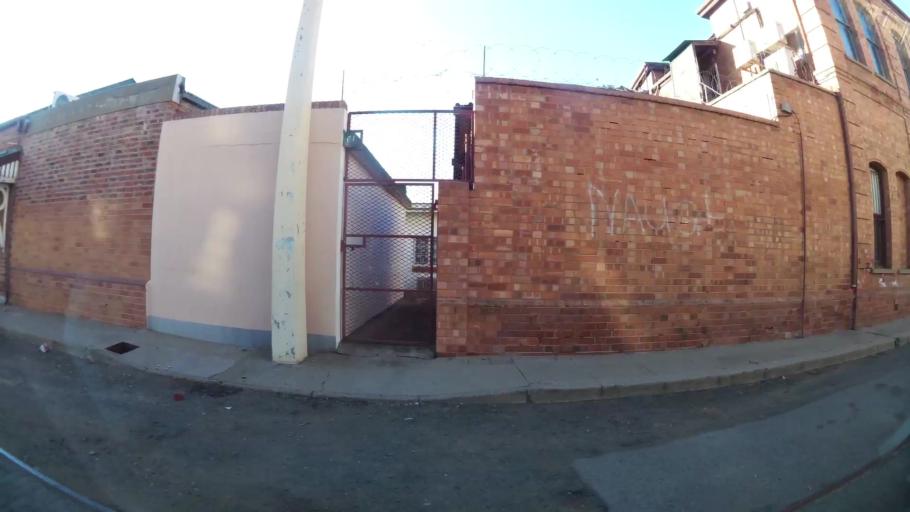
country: ZA
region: Northern Cape
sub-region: Frances Baard District Municipality
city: Kimberley
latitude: -28.7386
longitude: 24.7619
